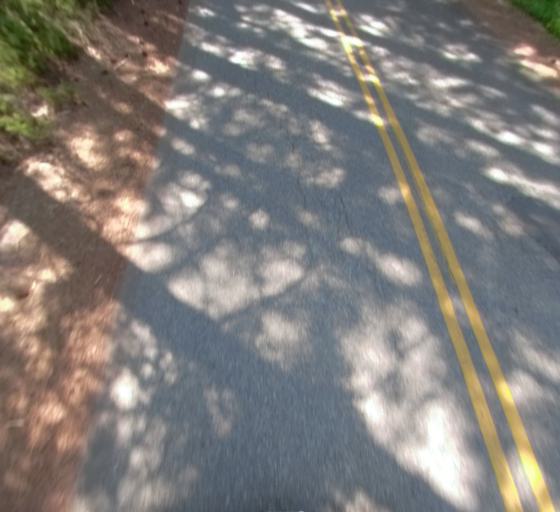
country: US
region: California
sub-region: Madera County
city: Oakhurst
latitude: 37.3491
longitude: -119.3870
